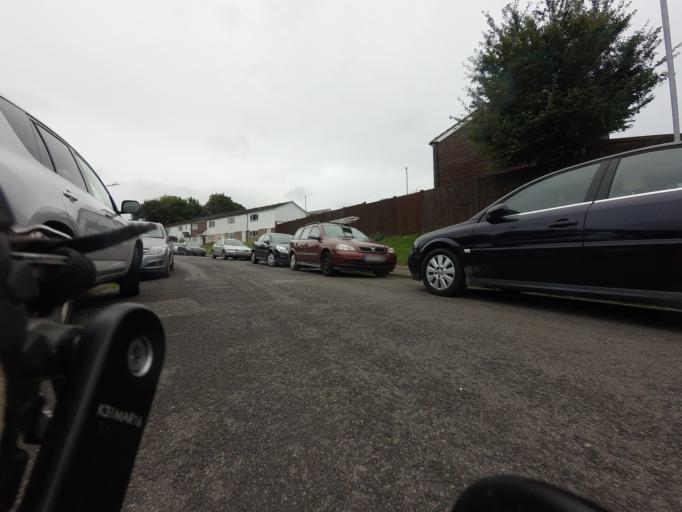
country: GB
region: England
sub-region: Kent
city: Swanley
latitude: 51.4009
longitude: 0.1767
